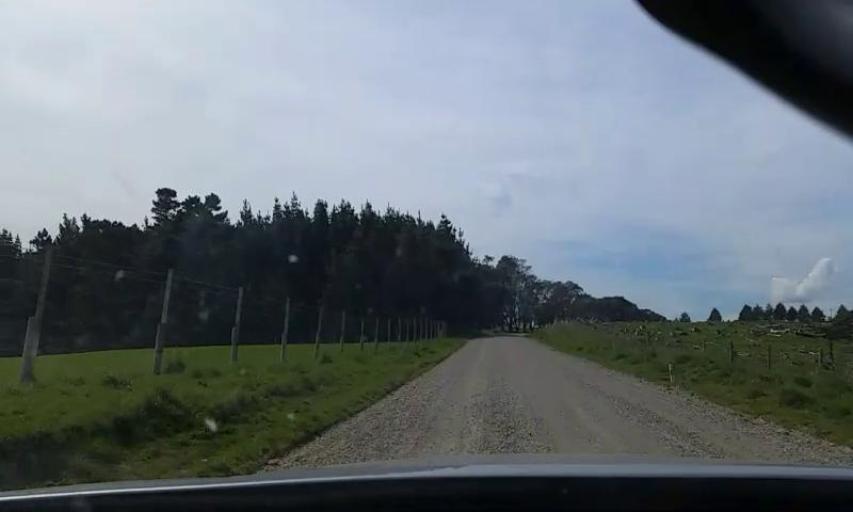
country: NZ
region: Otago
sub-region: Clutha District
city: Papatowai
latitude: -46.6332
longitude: 168.9743
